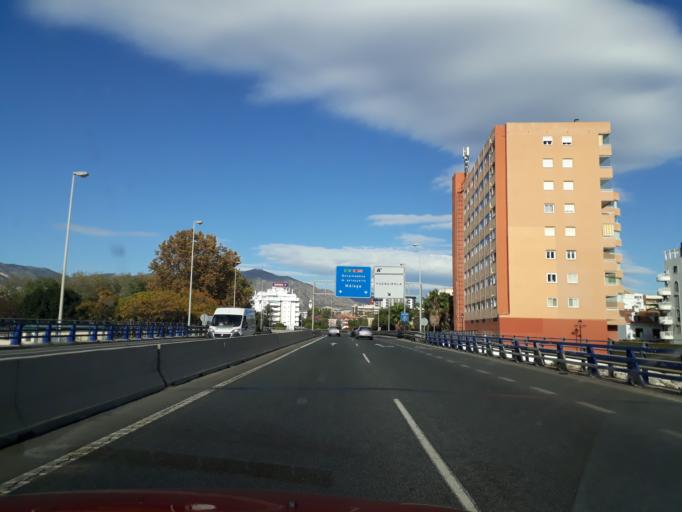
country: ES
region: Andalusia
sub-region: Provincia de Malaga
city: Fuengirola
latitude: 36.5270
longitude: -4.6293
